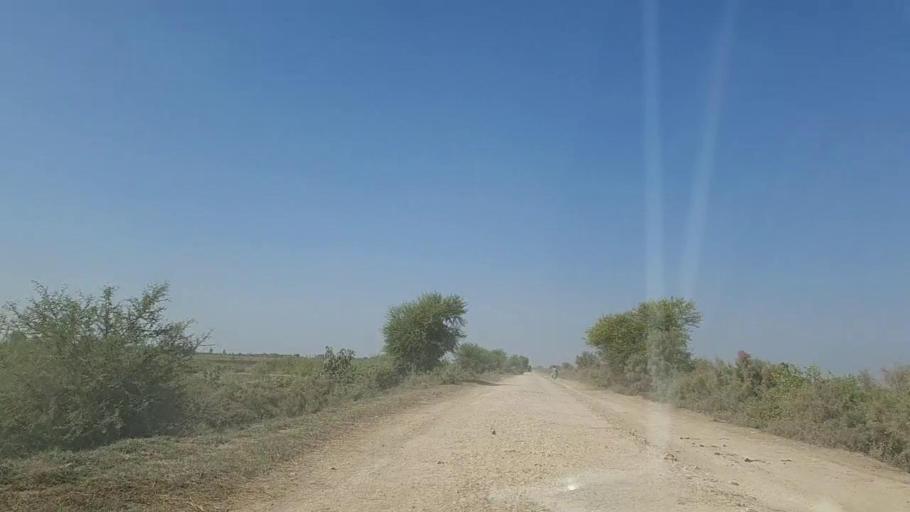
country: PK
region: Sindh
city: Chuhar Jamali
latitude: 24.4204
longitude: 68.0142
